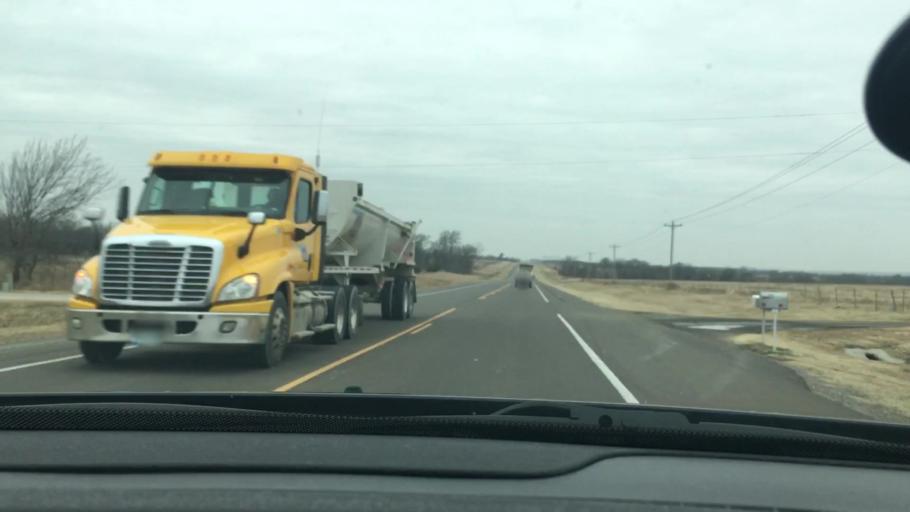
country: US
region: Oklahoma
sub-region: Murray County
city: Davis
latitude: 34.5213
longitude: -97.2297
